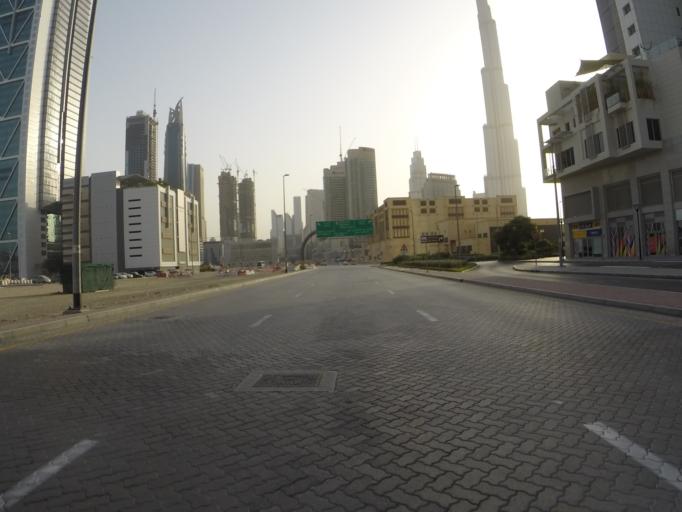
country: AE
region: Dubai
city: Dubai
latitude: 25.1928
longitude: 55.2658
